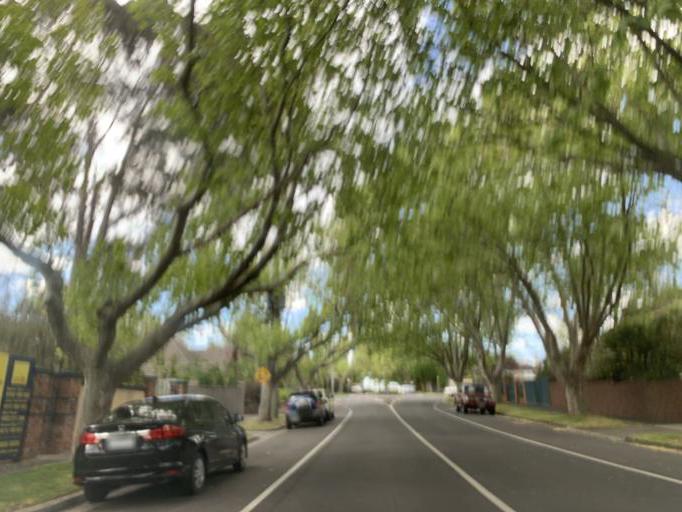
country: AU
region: Victoria
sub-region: Bayside
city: North Brighton
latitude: -37.9194
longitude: 144.9974
